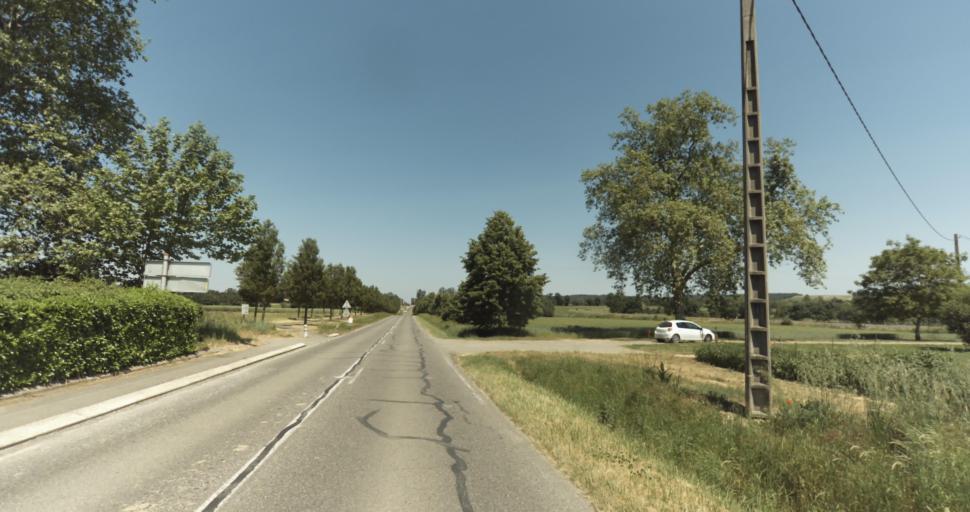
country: FR
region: Midi-Pyrenees
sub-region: Departement du Gers
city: Pujaudran
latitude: 43.6391
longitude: 1.1551
